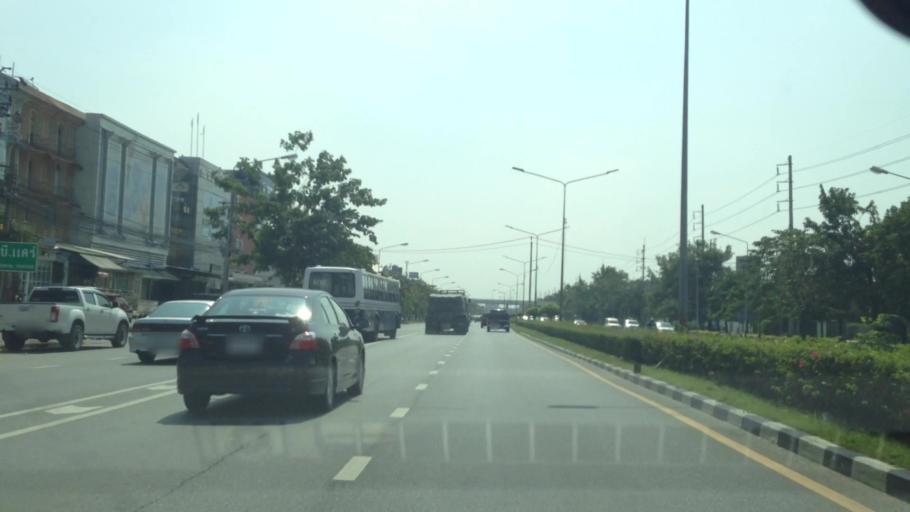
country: TH
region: Bangkok
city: Sai Mai
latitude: 13.9430
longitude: 100.6237
